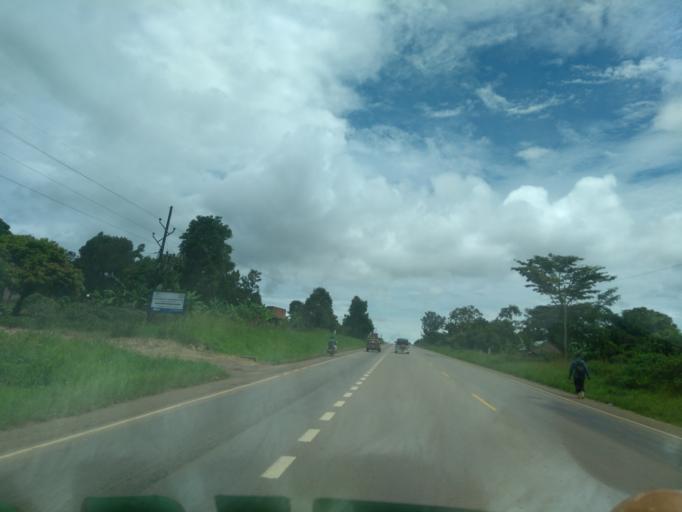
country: UG
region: Central Region
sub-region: Butambala District
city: Gombe
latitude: 0.0072
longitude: 32.0466
